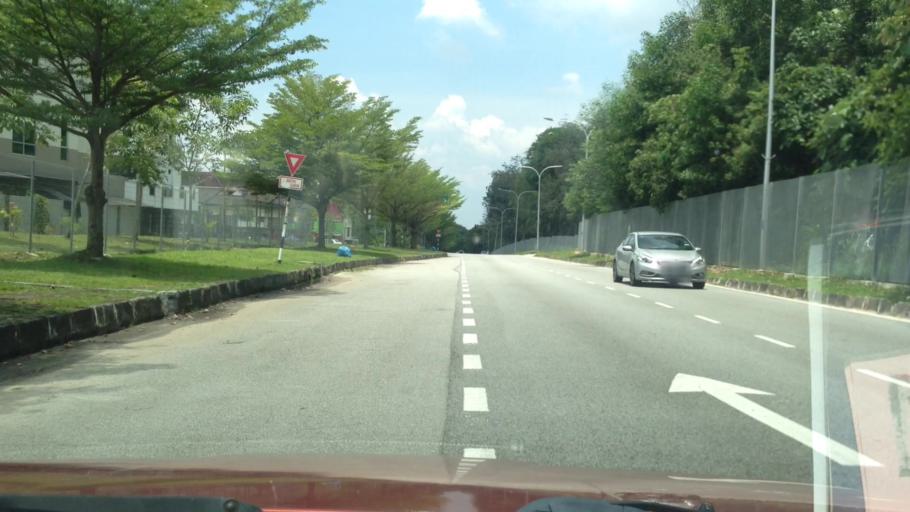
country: MY
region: Selangor
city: Kampung Baru Subang
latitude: 3.1665
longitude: 101.5516
